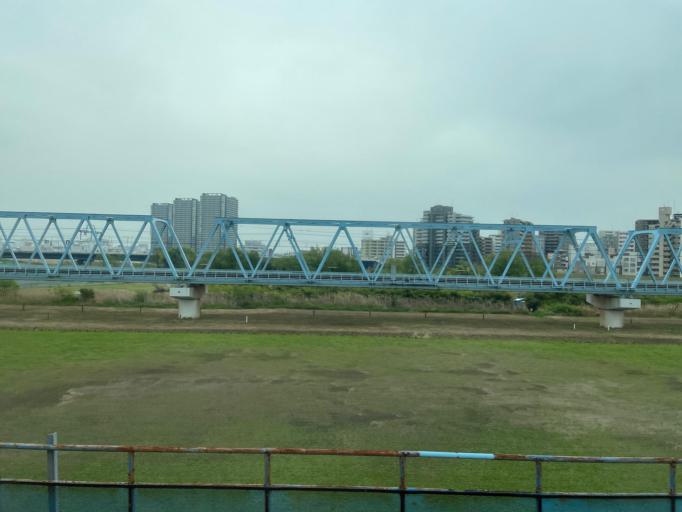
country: JP
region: Kanagawa
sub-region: Kawasaki-shi
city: Kawasaki
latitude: 35.5383
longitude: 139.7043
